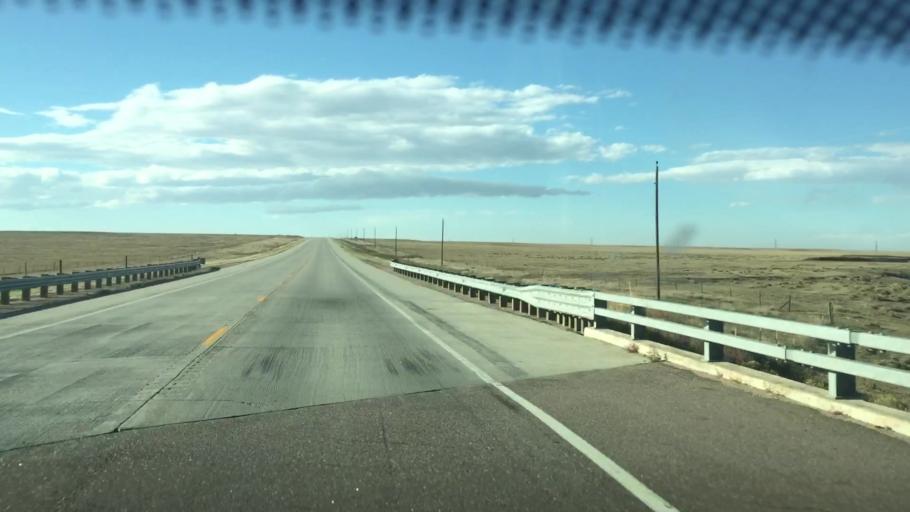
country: US
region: Colorado
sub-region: Lincoln County
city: Hugo
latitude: 39.0704
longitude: -103.3745
